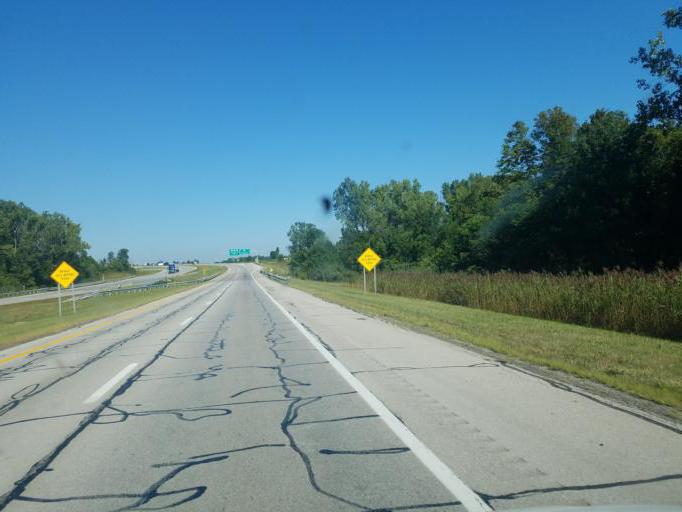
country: US
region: Ohio
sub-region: Crawford County
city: Bucyrus
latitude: 40.8217
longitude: -82.9454
